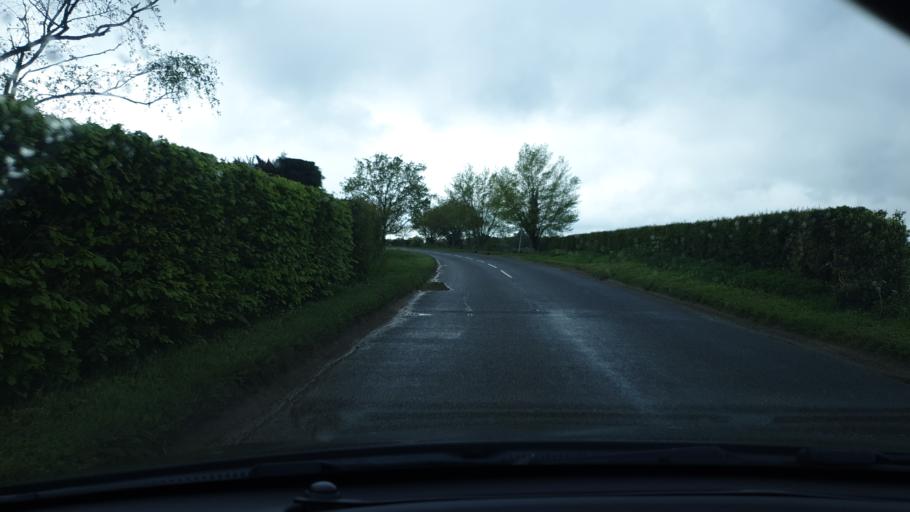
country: GB
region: England
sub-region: Essex
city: Wivenhoe
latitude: 51.9079
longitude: 0.9768
